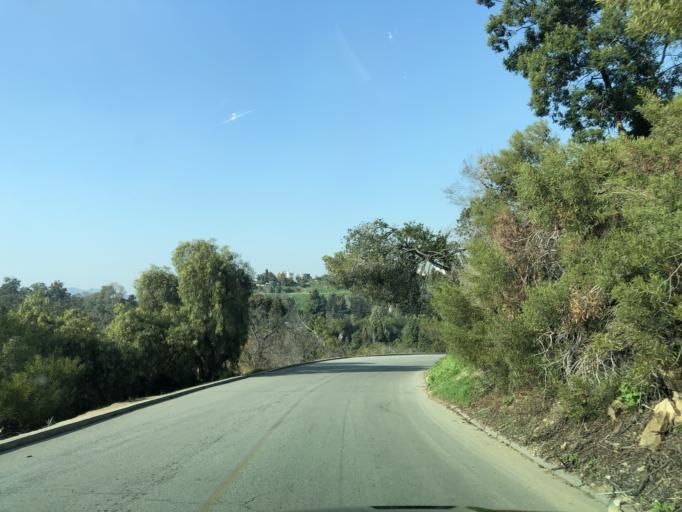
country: US
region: California
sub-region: Los Angeles County
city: Echo Park
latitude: 34.0830
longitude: -118.2442
